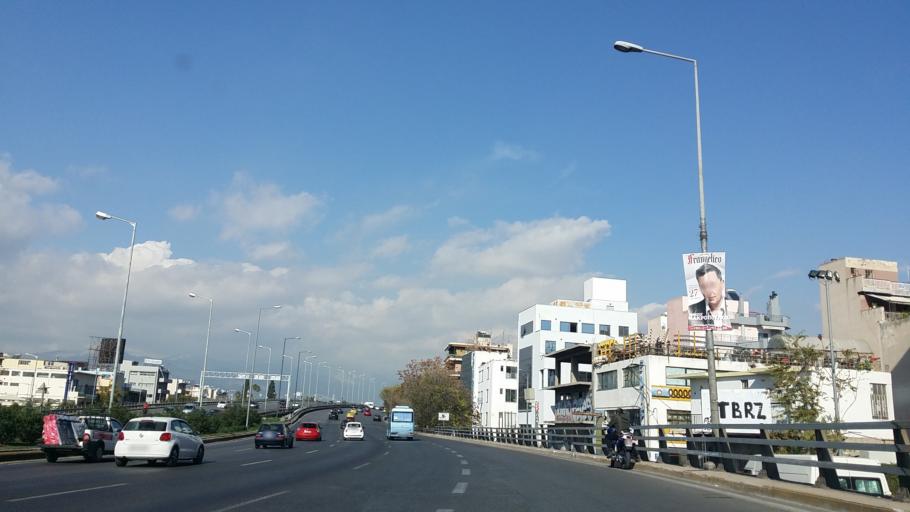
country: GR
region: Attica
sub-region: Nomarchia Athinas
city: Agioi Anargyroi
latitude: 38.0107
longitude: 23.7181
